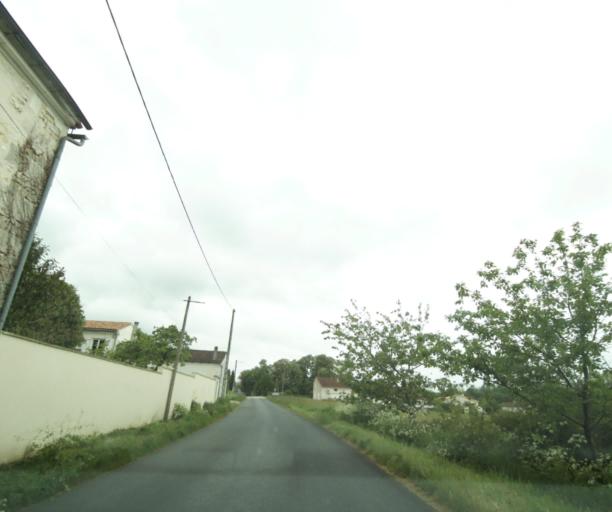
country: FR
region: Poitou-Charentes
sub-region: Departement de la Charente-Maritime
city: Chaniers
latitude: 45.6998
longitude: -0.5451
